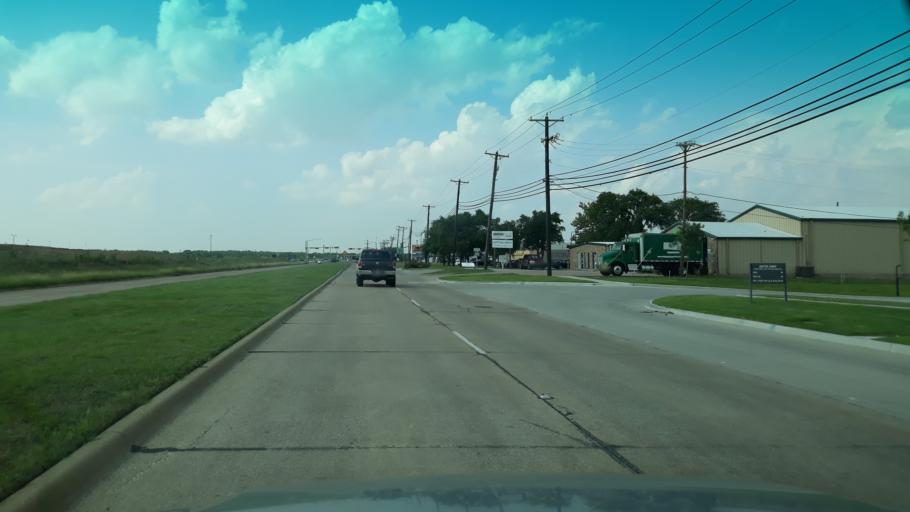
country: US
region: Texas
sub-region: Tarrant County
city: Euless
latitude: 32.8543
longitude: -97.0214
